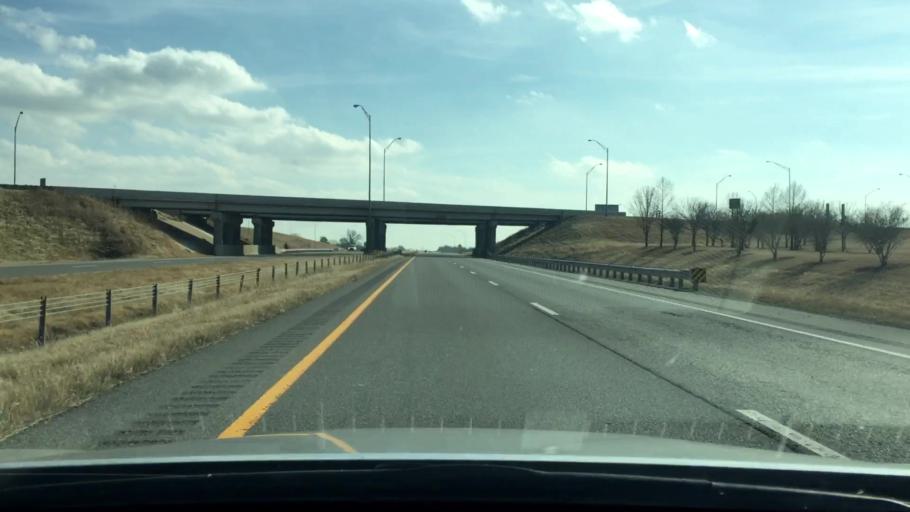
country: US
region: Oklahoma
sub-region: McClain County
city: Purcell
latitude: 34.9837
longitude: -97.3729
